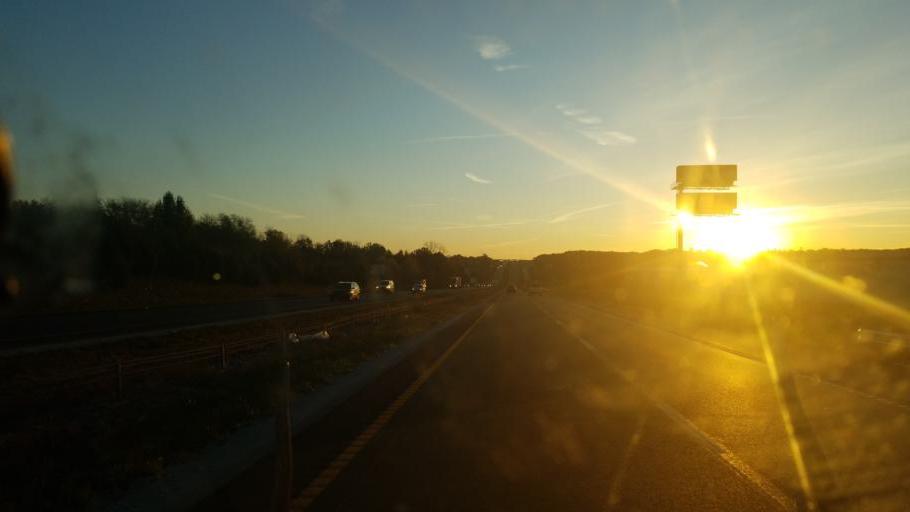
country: US
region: Missouri
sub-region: Boone County
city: Columbia
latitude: 38.9610
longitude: -92.2749
